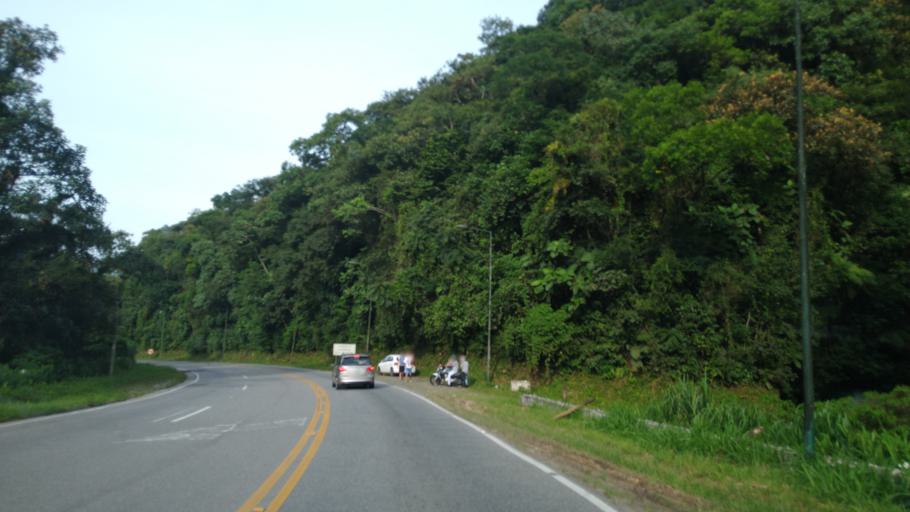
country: BR
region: Santa Catarina
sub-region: Joinville
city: Joinville
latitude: -26.1916
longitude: -49.0303
